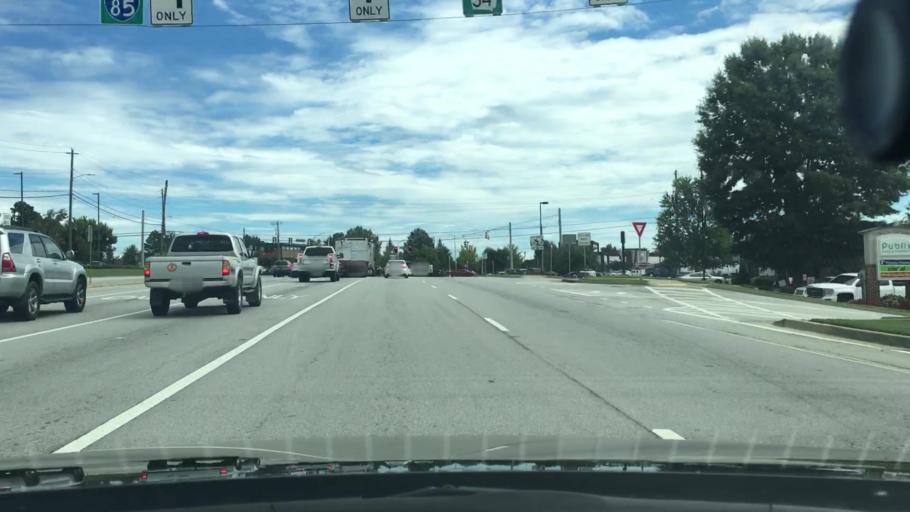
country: US
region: Georgia
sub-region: Coweta County
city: Newnan
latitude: 33.3963
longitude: -84.7632
